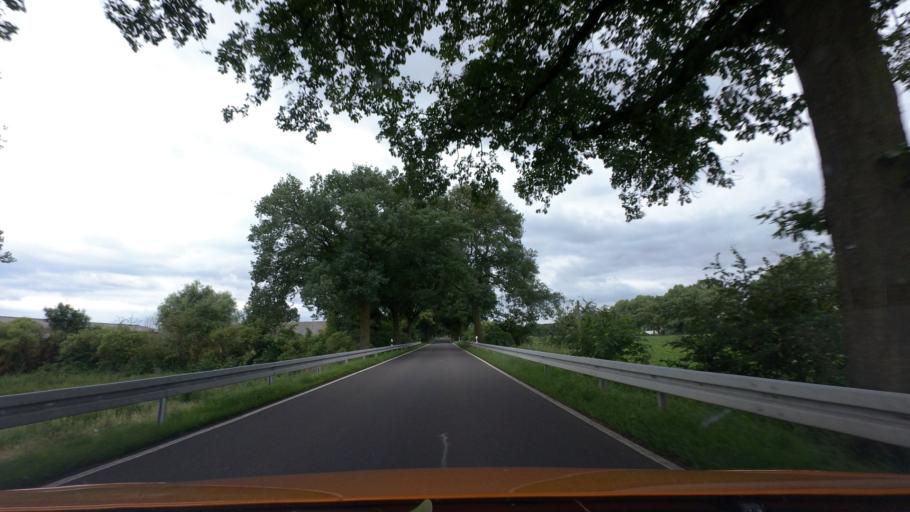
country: DE
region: Brandenburg
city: Neulewin
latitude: 52.7415
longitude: 14.2426
